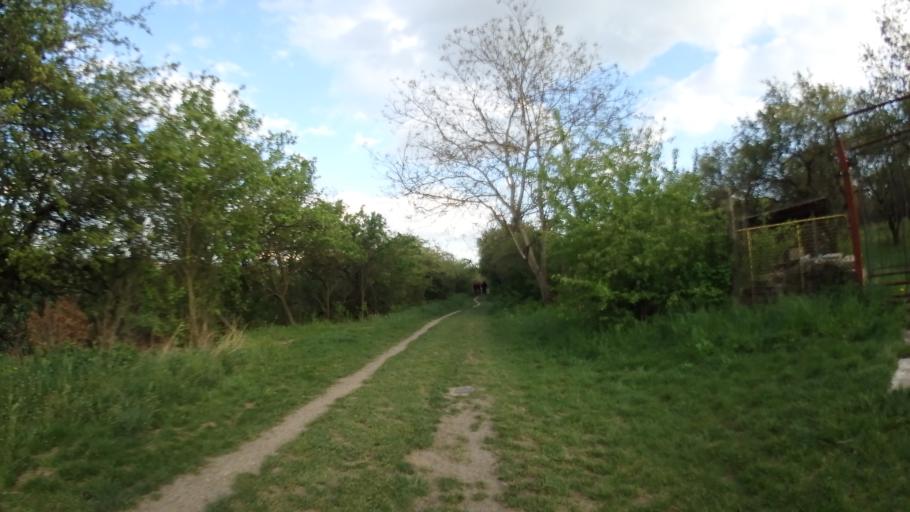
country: CZ
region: South Moravian
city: Moravany
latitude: 49.1587
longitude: 16.5748
